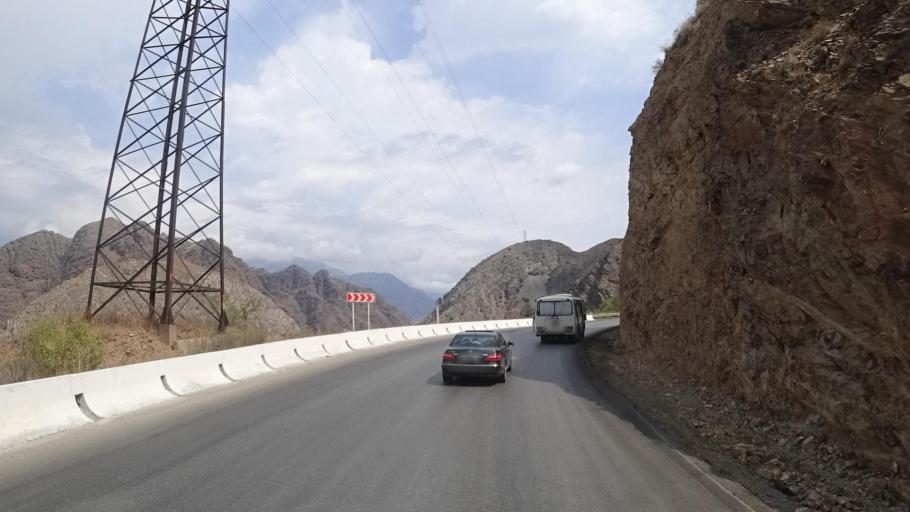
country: KG
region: Jalal-Abad
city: Tash-Kumyr
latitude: 41.5732
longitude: 72.5333
